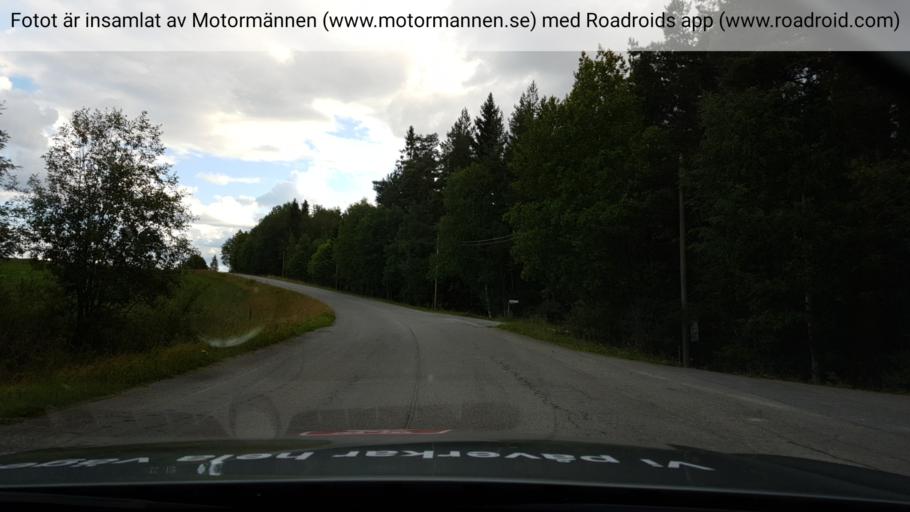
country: SE
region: Jaemtland
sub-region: Krokoms Kommun
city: Krokom
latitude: 63.2052
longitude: 14.4679
